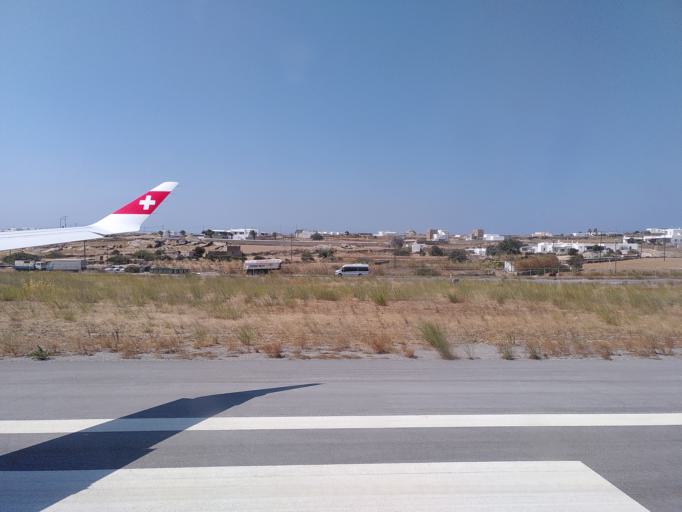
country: GR
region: South Aegean
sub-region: Nomos Kykladon
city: Mykonos
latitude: 37.4285
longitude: 25.3512
